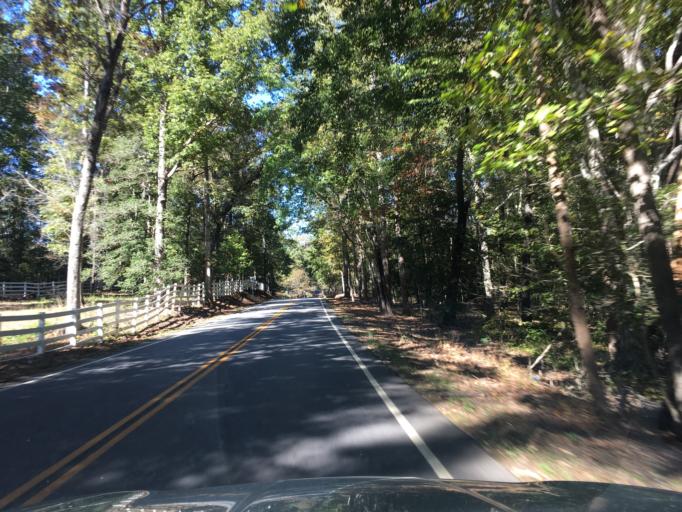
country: US
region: South Carolina
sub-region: Spartanburg County
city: Wellford
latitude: 34.8811
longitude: -82.1021
